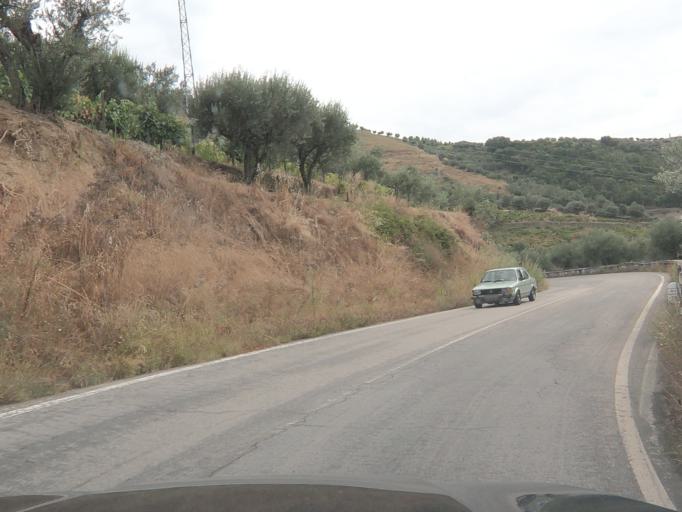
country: PT
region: Vila Real
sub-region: Santa Marta de Penaguiao
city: Santa Marta de Penaguiao
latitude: 41.2410
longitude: -7.7694
